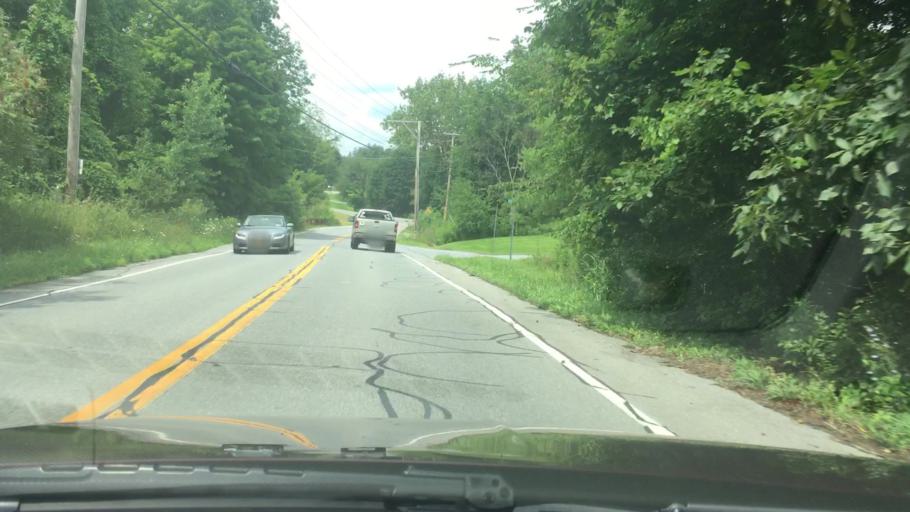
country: US
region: New York
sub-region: Dutchess County
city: Hillside Lake
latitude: 41.6512
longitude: -73.7465
